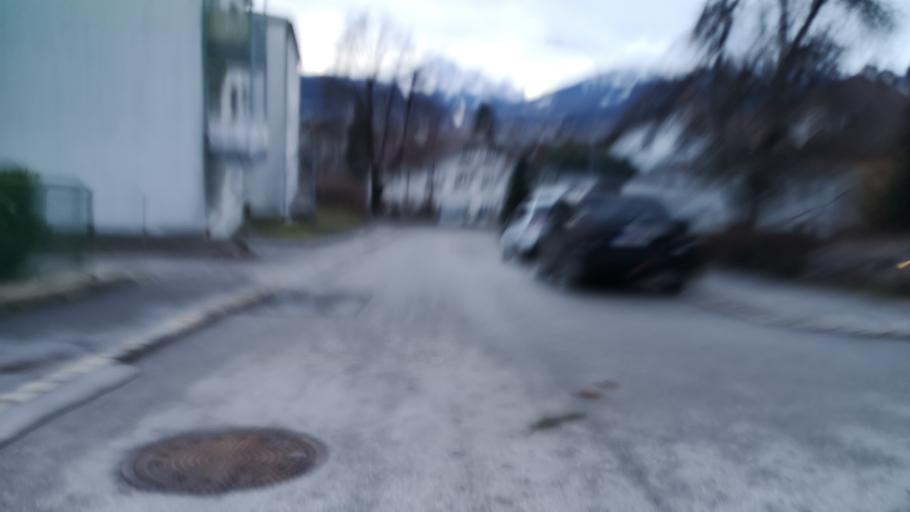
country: AT
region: Tyrol
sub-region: Innsbruck Stadt
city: Innsbruck
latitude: 47.2827
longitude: 11.4069
